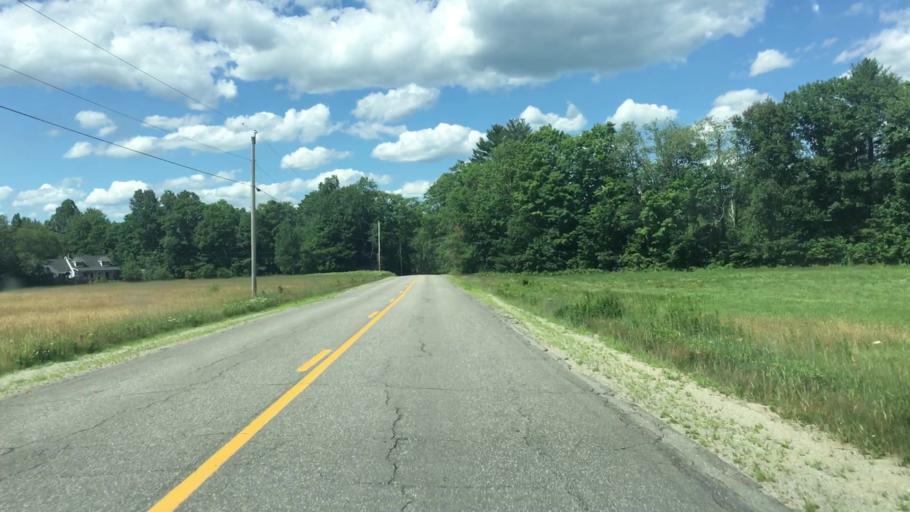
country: US
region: Maine
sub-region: Franklin County
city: Chesterville
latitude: 44.5846
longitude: -70.0891
